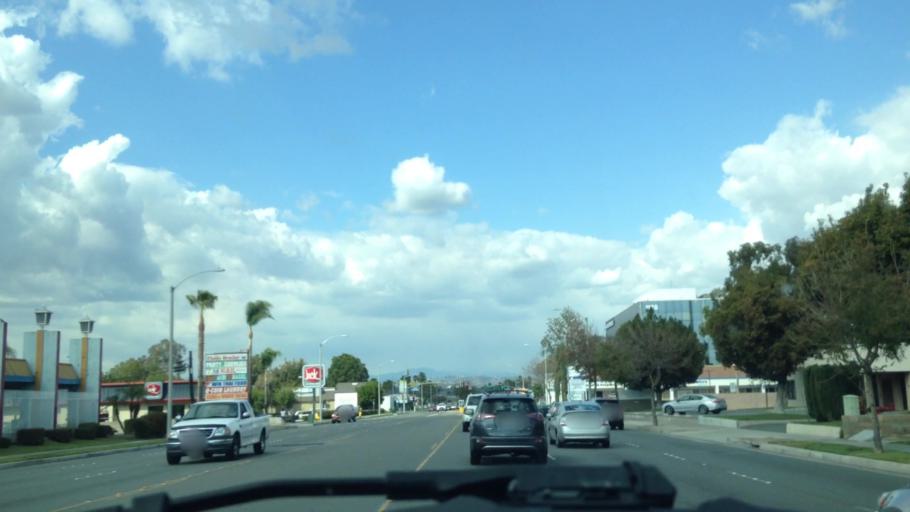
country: US
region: California
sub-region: Orange County
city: Fullerton
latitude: 33.8483
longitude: -117.9417
